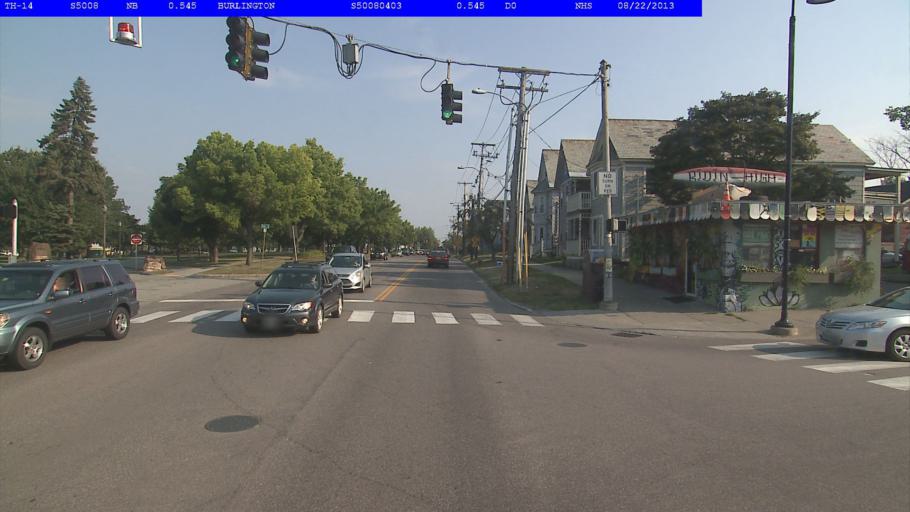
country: US
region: Vermont
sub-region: Chittenden County
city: Burlington
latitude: 44.4802
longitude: -73.2190
